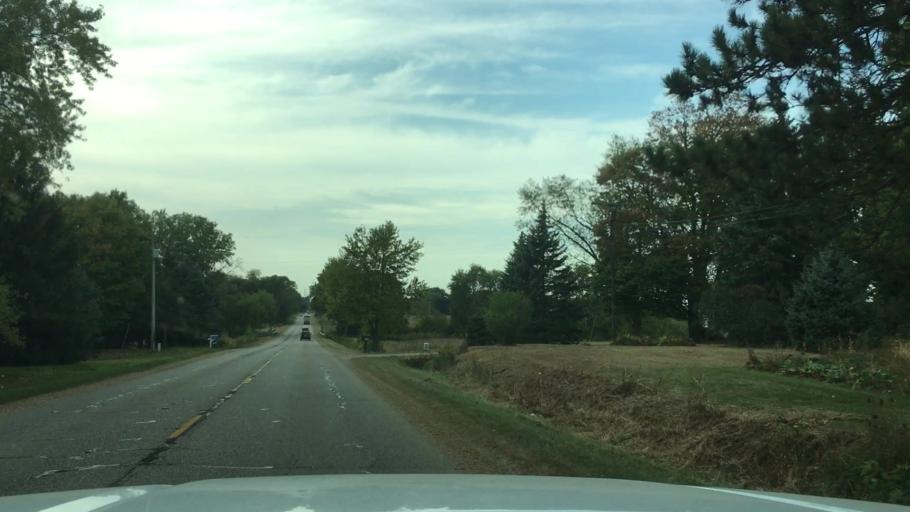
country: US
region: Michigan
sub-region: Ottawa County
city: Hudsonville
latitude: 42.7821
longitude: -85.8737
